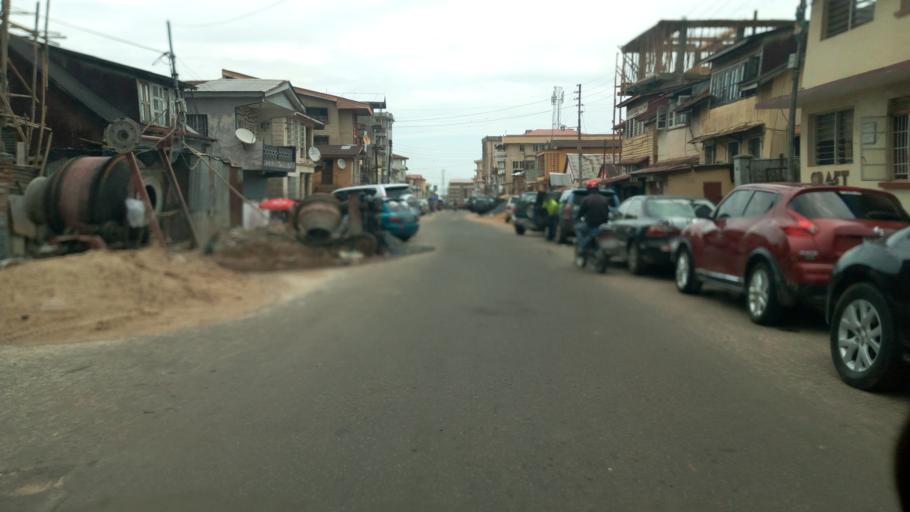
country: SL
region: Western Area
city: Freetown
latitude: 8.4833
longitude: -13.2368
